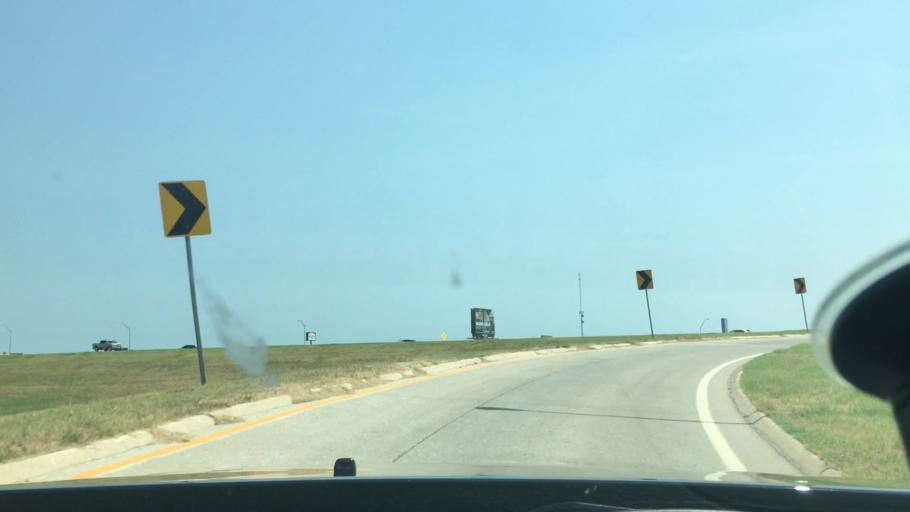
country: US
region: Oklahoma
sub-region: Carter County
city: Ardmore
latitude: 34.1740
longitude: -97.1696
